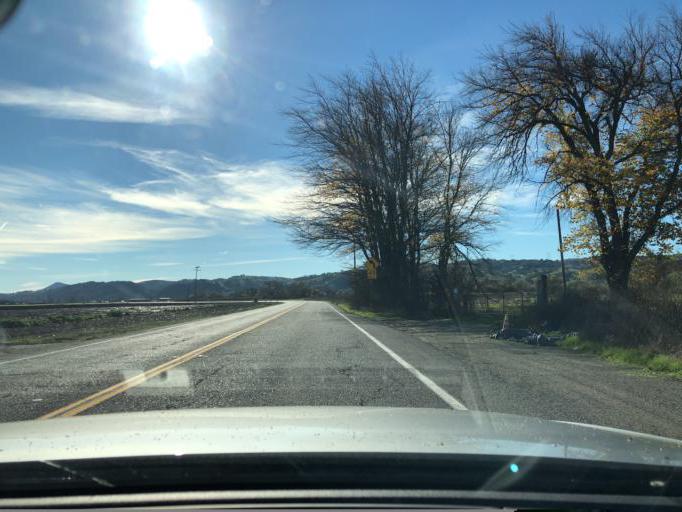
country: US
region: California
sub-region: Santa Clara County
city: Morgan Hill
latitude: 37.1954
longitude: -121.7345
